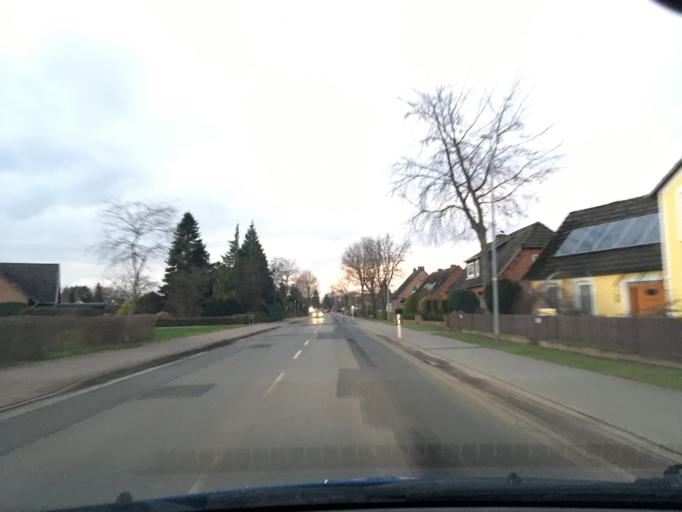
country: DE
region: Lower Saxony
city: Tespe
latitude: 53.3901
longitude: 10.4146
